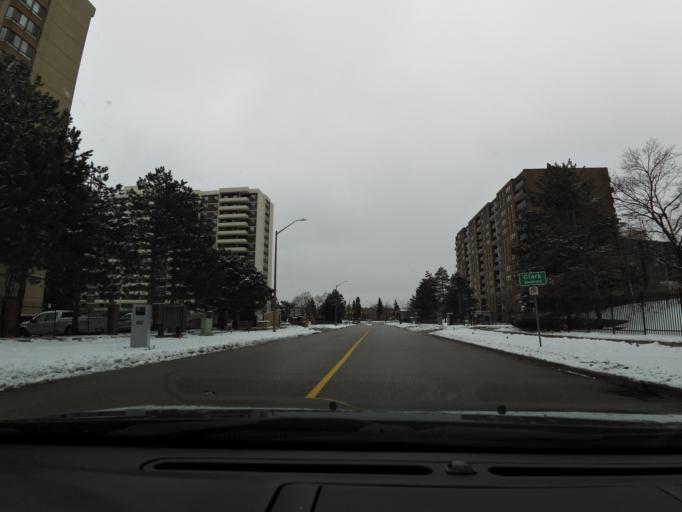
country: CA
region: Ontario
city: Brampton
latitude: 43.7107
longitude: -79.7258
